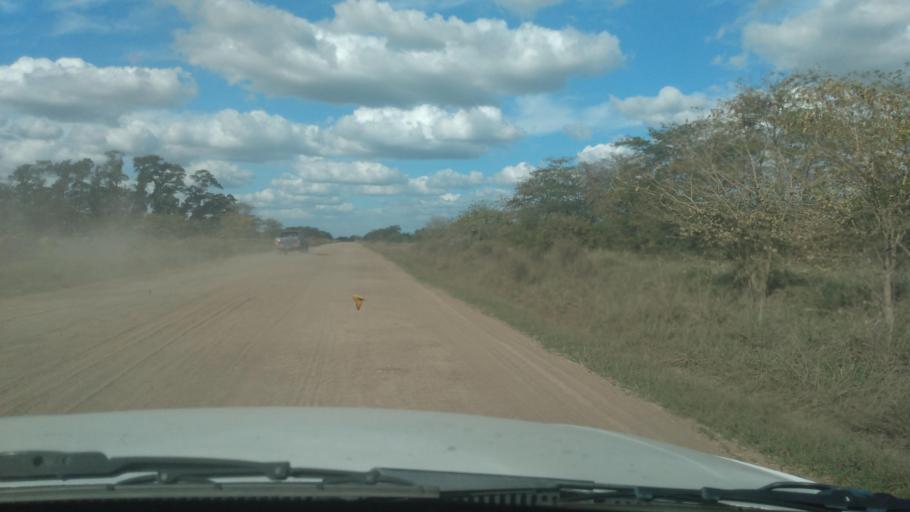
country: AR
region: Buenos Aires
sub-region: Partido de Navarro
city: Navarro
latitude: -35.0124
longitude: -59.4821
